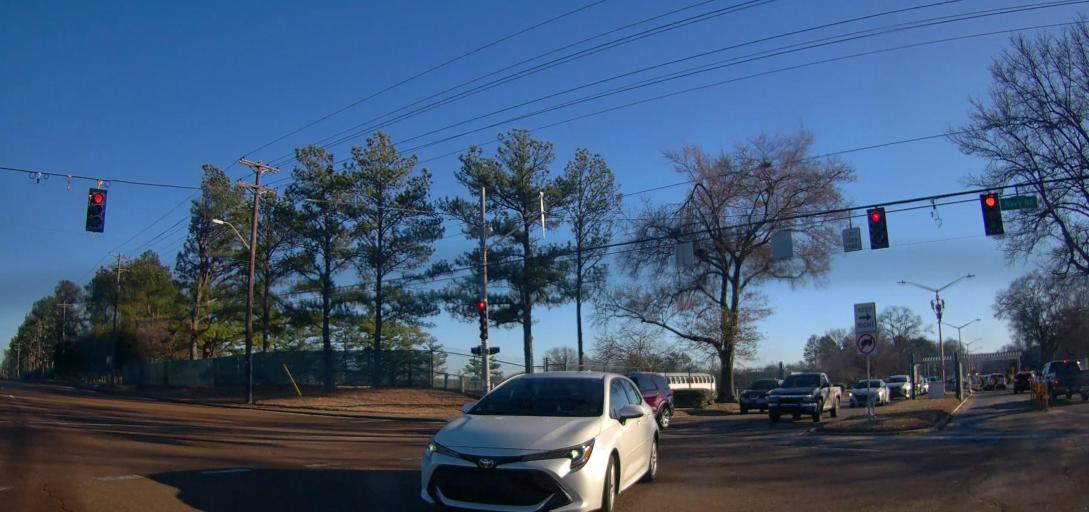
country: US
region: Tennessee
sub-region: Shelby County
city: Millington
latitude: 35.3402
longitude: -89.8777
